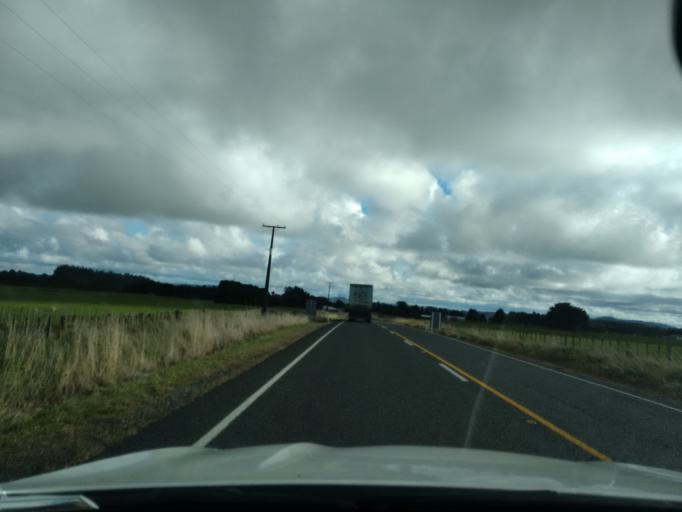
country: NZ
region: Manawatu-Wanganui
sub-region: Ruapehu District
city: Waiouru
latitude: -39.3564
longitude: 175.3531
